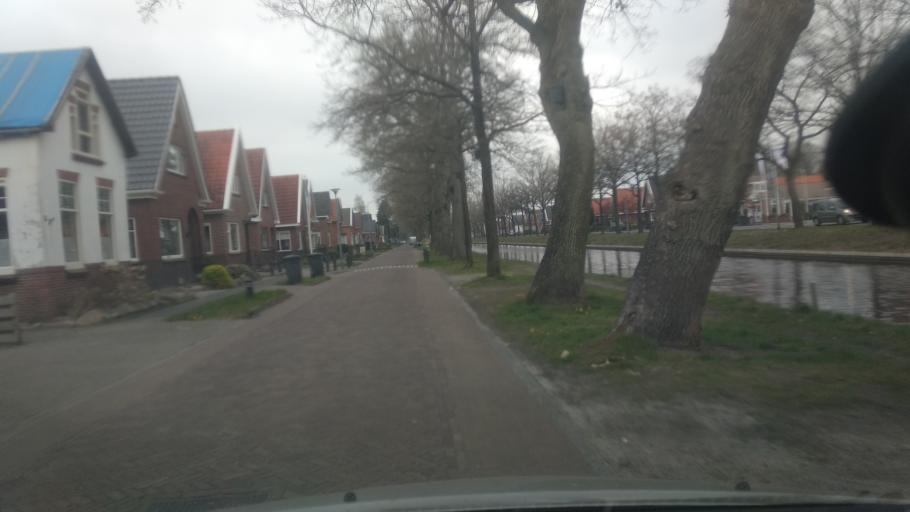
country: NL
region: Groningen
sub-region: Gemeente Stadskanaal
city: Stadskanaal
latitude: 52.9624
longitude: 6.9755
